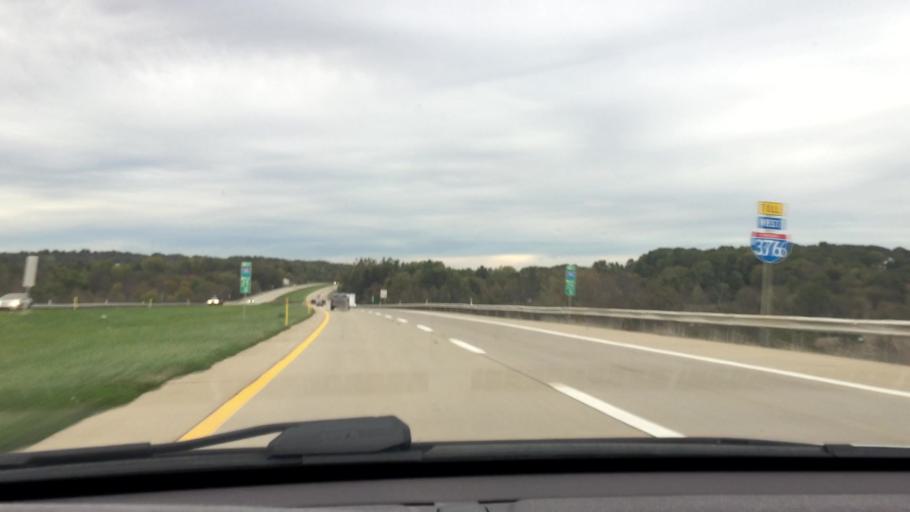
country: US
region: Pennsylvania
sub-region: Beaver County
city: Big Beaver
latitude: 40.8479
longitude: -80.3679
